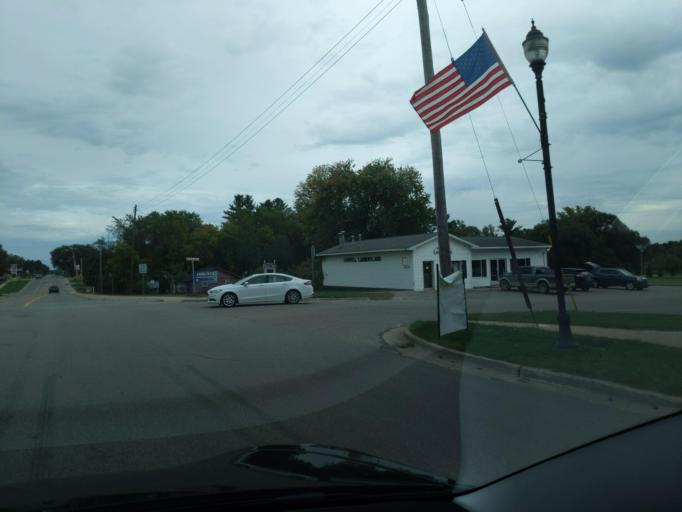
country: US
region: Michigan
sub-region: Clare County
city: Clare
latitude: 43.8349
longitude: -84.8657
